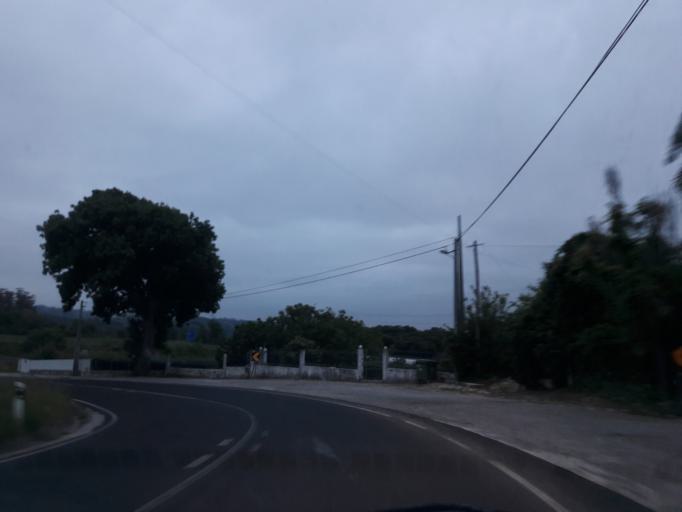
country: PT
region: Leiria
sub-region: Obidos
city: Obidos
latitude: 39.3725
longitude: -9.1332
